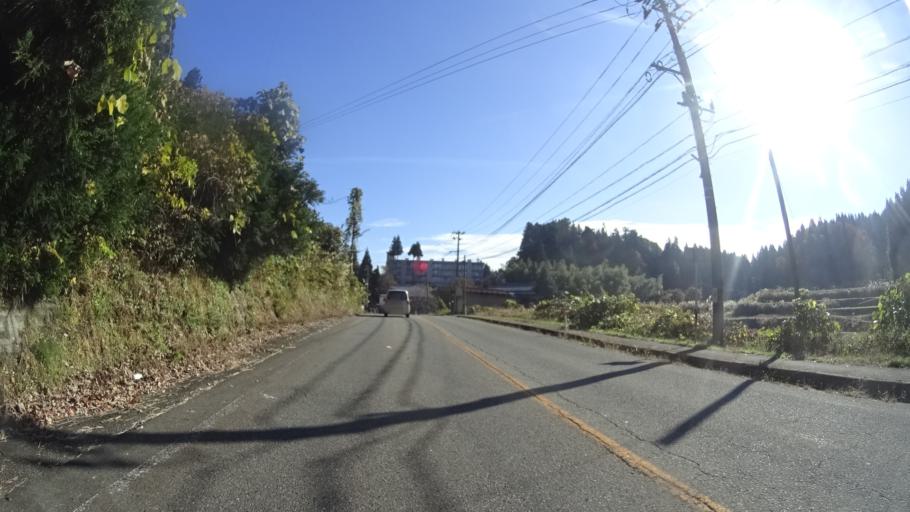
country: JP
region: Niigata
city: Tochio-honcho
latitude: 37.4830
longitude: 138.9853
